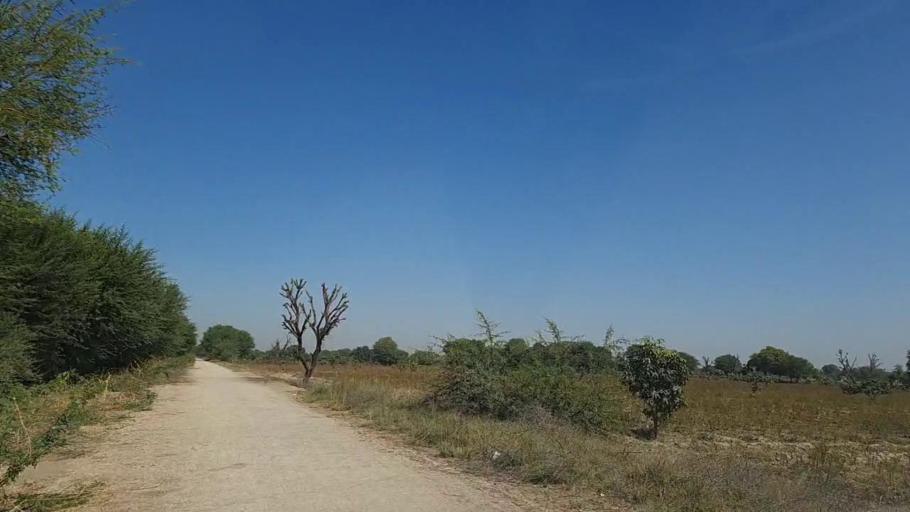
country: PK
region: Sindh
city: Samaro
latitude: 25.3545
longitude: 69.5227
